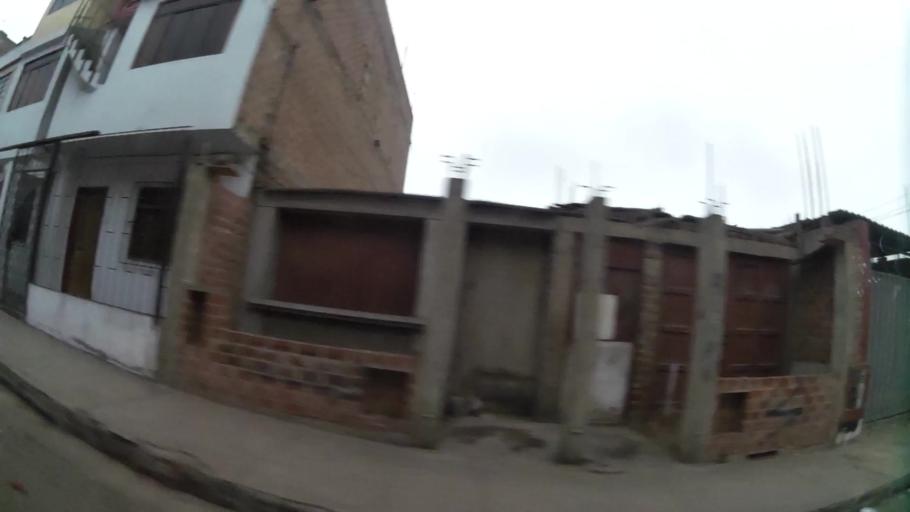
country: PE
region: Lima
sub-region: Lima
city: Surco
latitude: -12.1469
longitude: -76.9716
